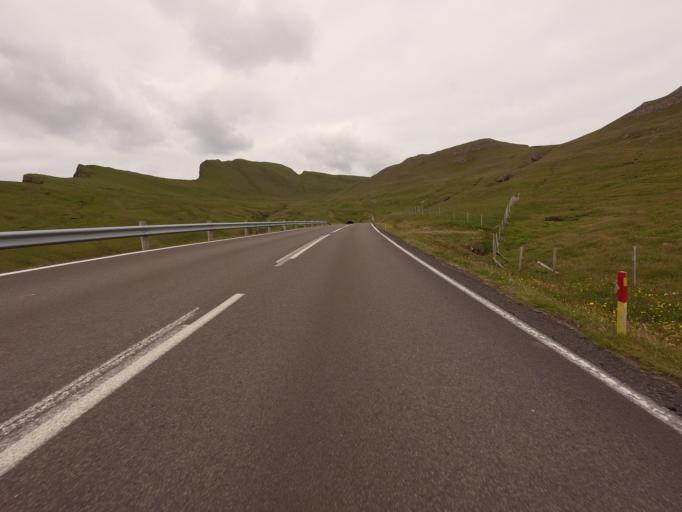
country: FO
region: Suduroy
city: Vagur
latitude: 61.4109
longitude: -6.7425
